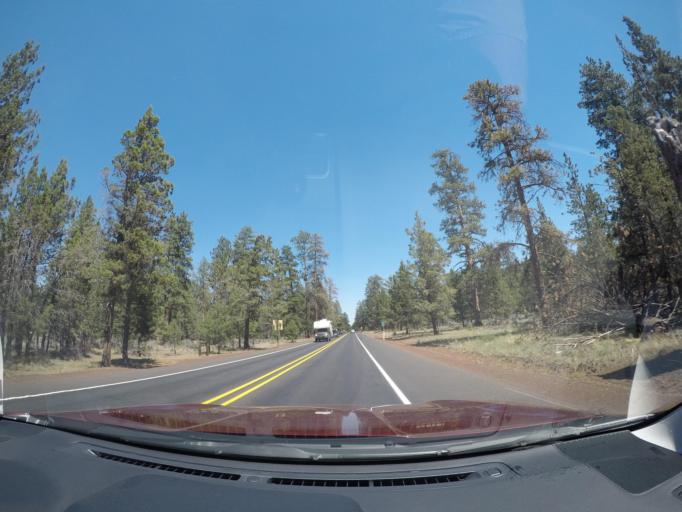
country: US
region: Oregon
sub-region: Deschutes County
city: Sisters
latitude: 44.2877
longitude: -121.5368
